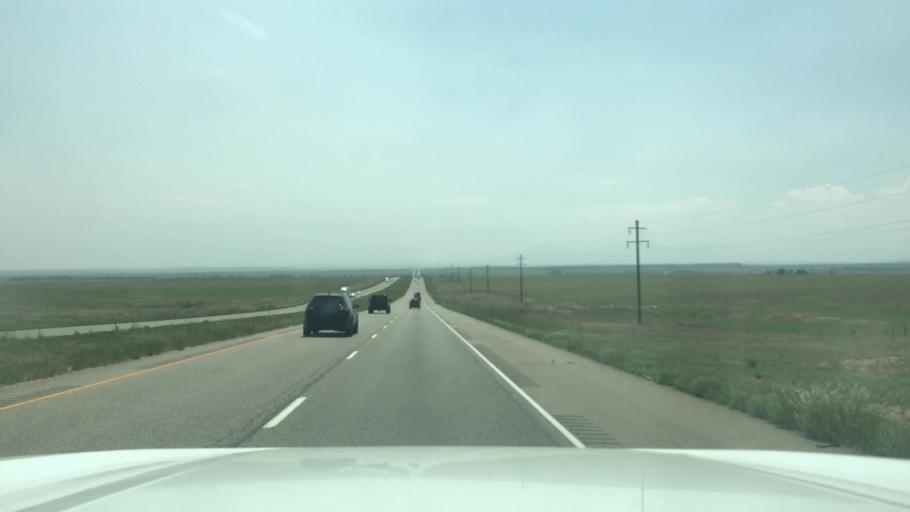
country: US
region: Colorado
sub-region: Pueblo County
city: Colorado City
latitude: 37.8839
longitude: -104.8295
